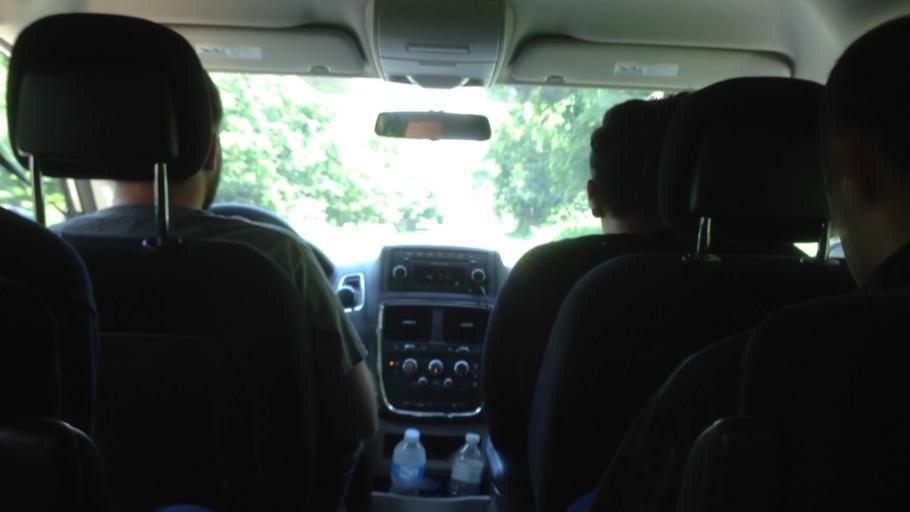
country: US
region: New York
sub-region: Dutchess County
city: Tivoli
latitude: 42.0969
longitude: -73.8963
